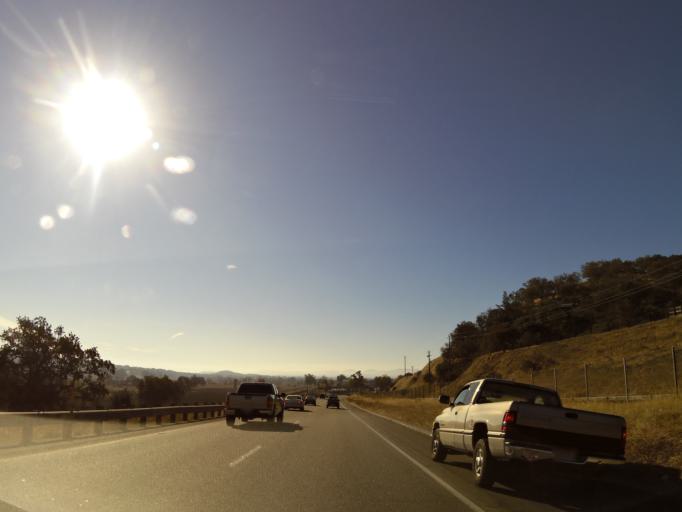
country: US
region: California
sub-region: San Luis Obispo County
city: Paso Robles
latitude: 35.6048
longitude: -120.6926
